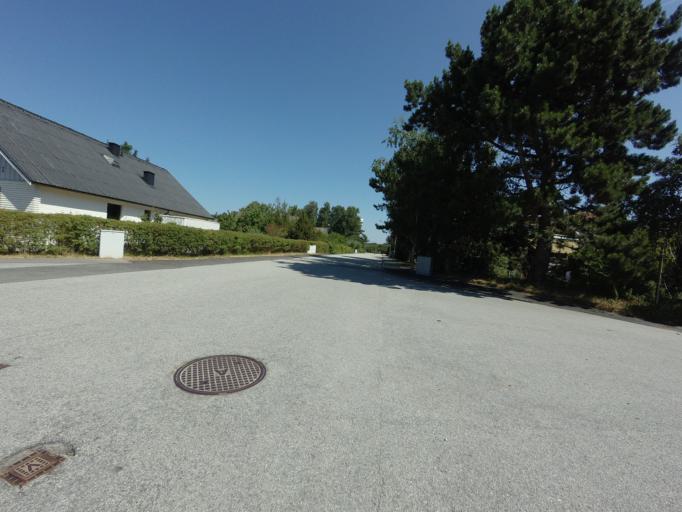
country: SE
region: Skane
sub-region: Vellinge Kommun
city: Skanor med Falsterbo
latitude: 55.4003
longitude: 12.8424
